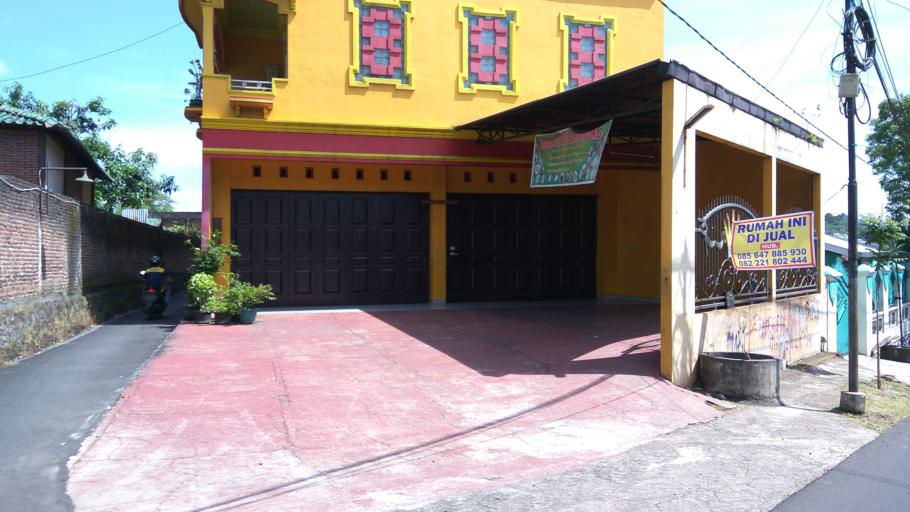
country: ID
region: Central Java
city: Ungaran
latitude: -7.1191
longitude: 110.4045
